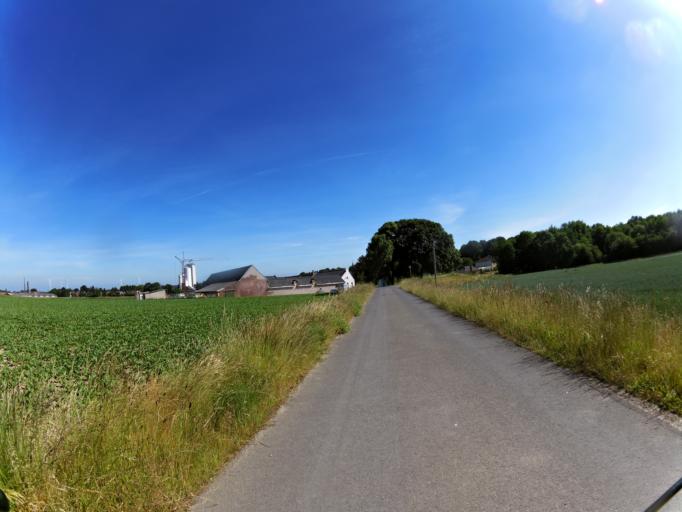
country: DE
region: North Rhine-Westphalia
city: Geilenkirchen
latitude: 50.9763
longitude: 6.0734
